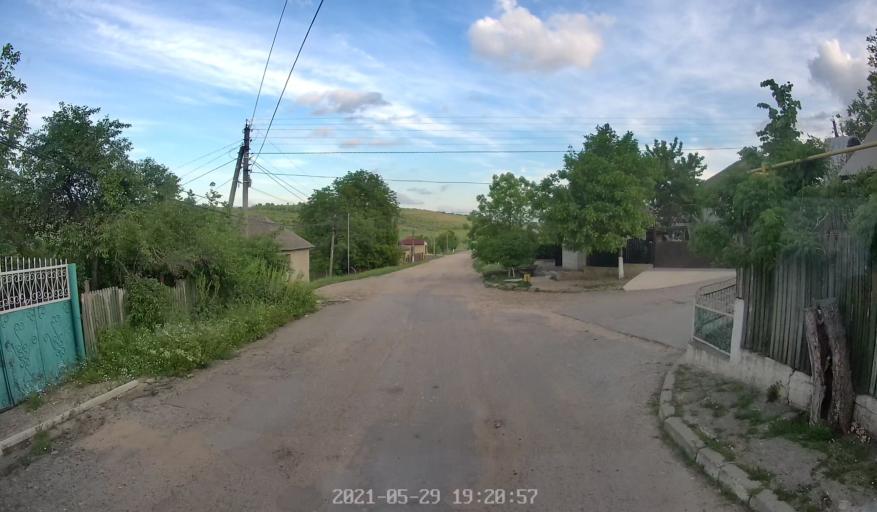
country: MD
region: Chisinau
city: Singera
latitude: 46.8387
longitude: 28.9539
